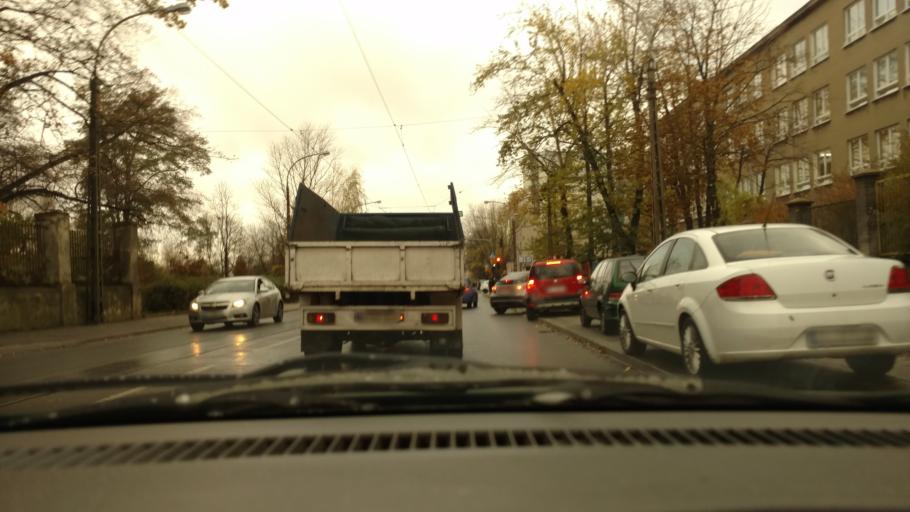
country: PL
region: Lodz Voivodeship
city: Lodz
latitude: 51.7781
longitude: 19.4910
